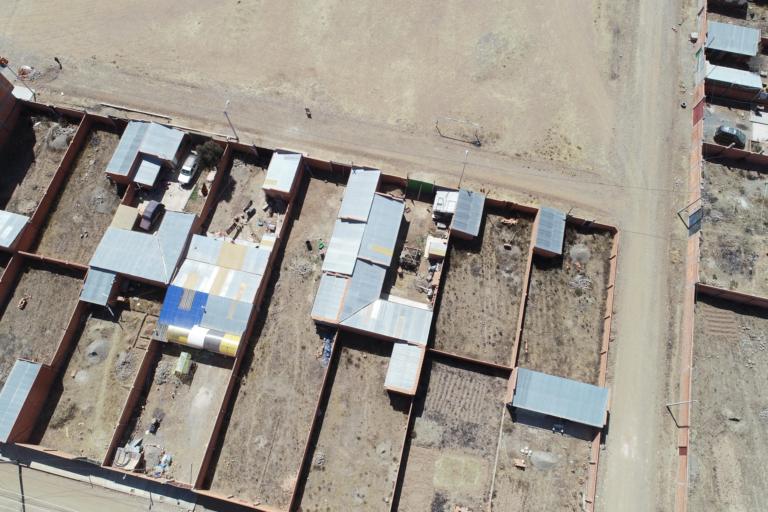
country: BO
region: La Paz
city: La Paz
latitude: -16.5928
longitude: -68.2106
